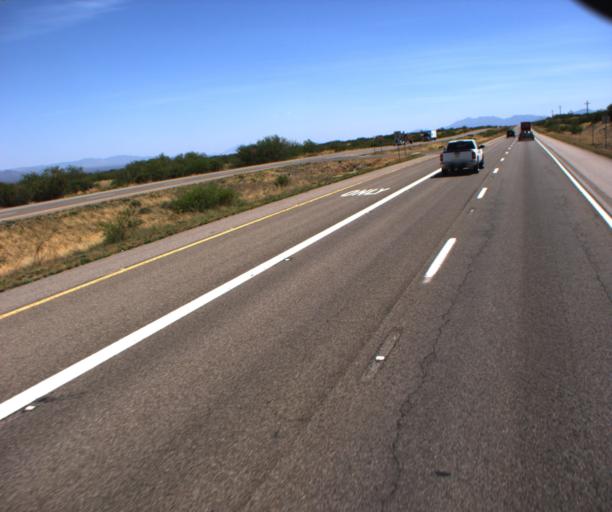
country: US
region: Arizona
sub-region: Cochise County
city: Whetstone
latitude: 31.8824
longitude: -110.3413
